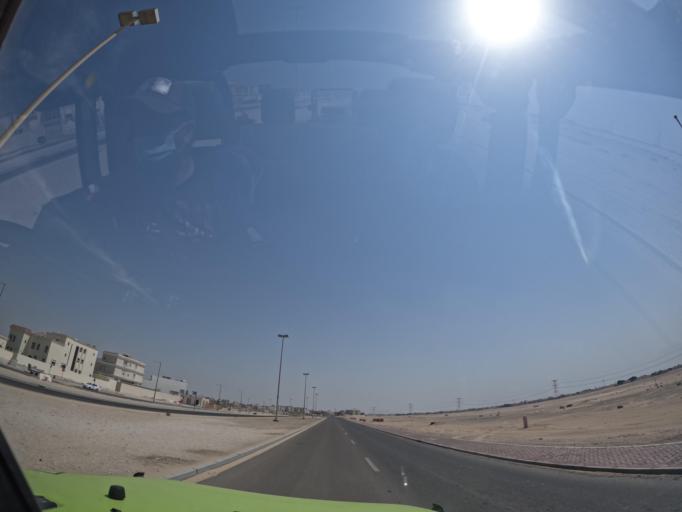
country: AE
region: Abu Dhabi
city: Abu Dhabi
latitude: 24.3049
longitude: 54.5462
